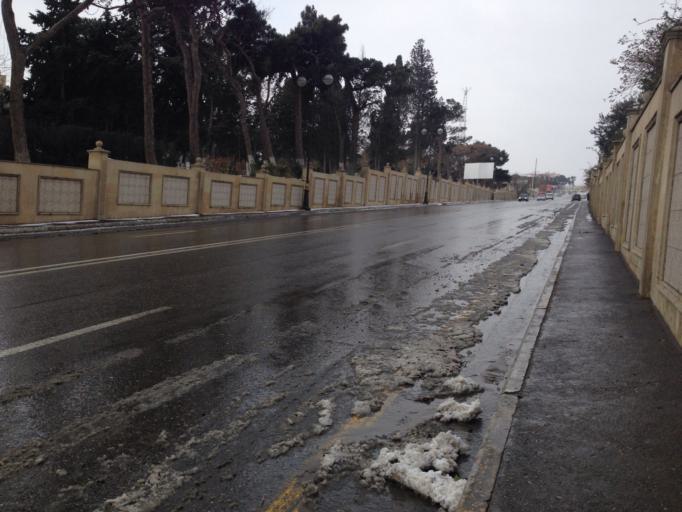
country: AZ
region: Baki
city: Baku
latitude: 40.3929
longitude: 49.8561
